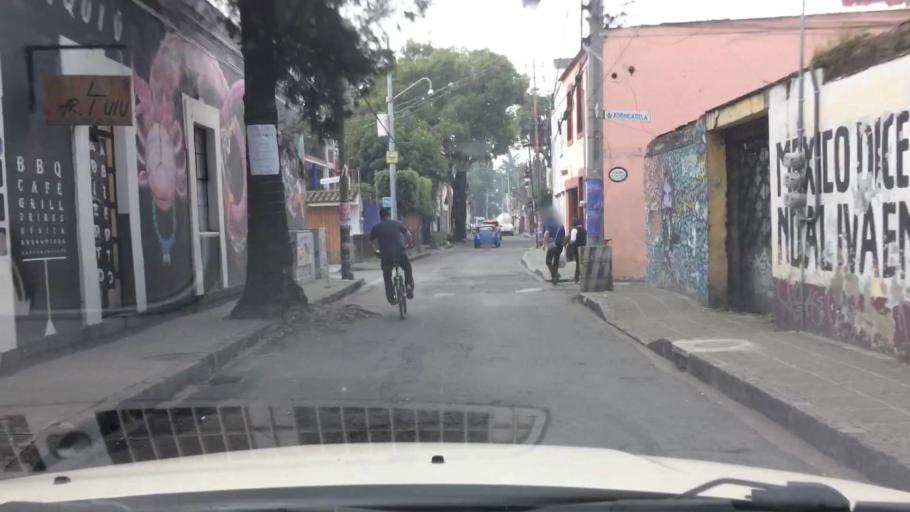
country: MX
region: Mexico City
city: Coyoacan
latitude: 19.3466
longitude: -99.1648
